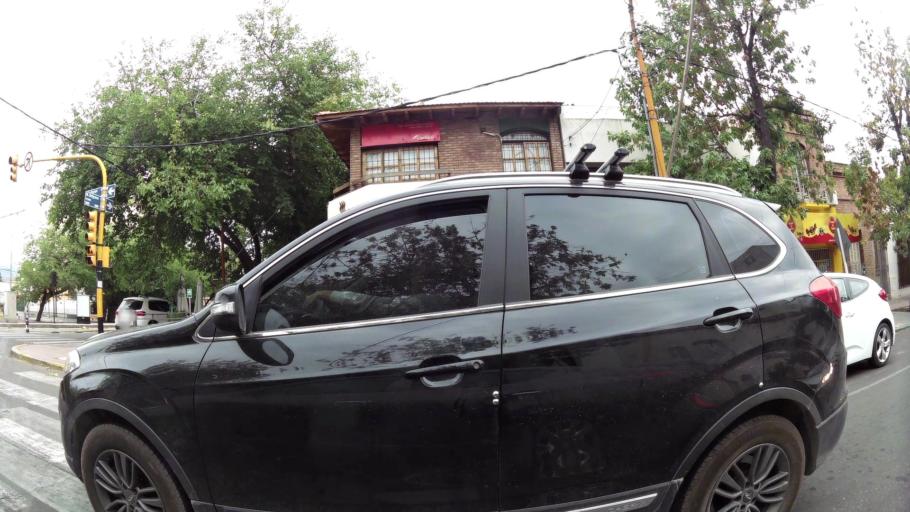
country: AR
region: Mendoza
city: Mendoza
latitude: -32.8876
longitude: -68.8506
